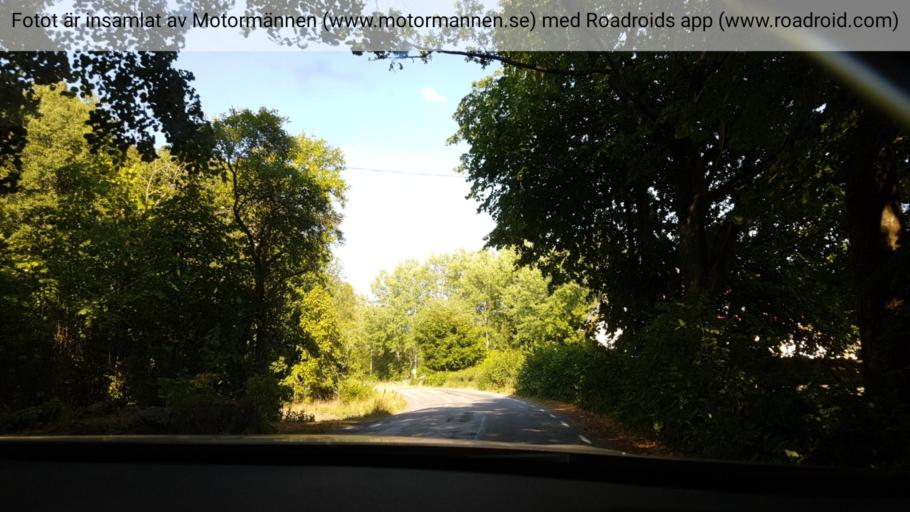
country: SE
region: Vaestra Goetaland
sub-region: Mariestads Kommun
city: Mariestad
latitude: 58.6107
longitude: 13.8770
